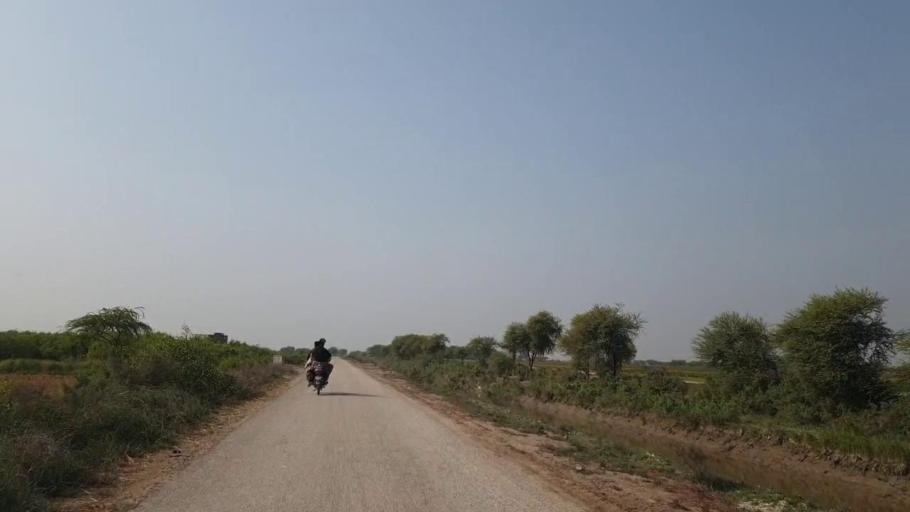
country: PK
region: Sindh
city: Kario
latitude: 24.9462
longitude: 68.5329
